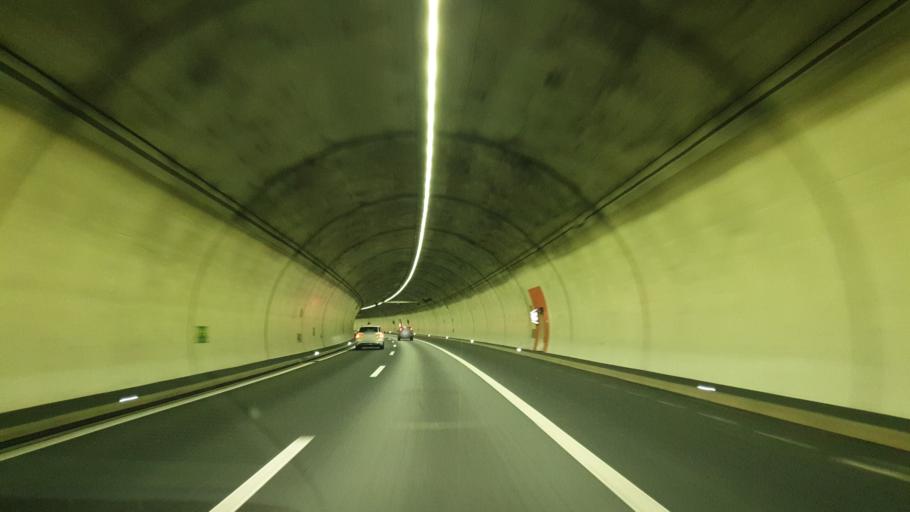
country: CH
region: Zurich
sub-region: Bezirk Dietikon
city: Birmensdorf
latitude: 47.3547
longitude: 8.4243
